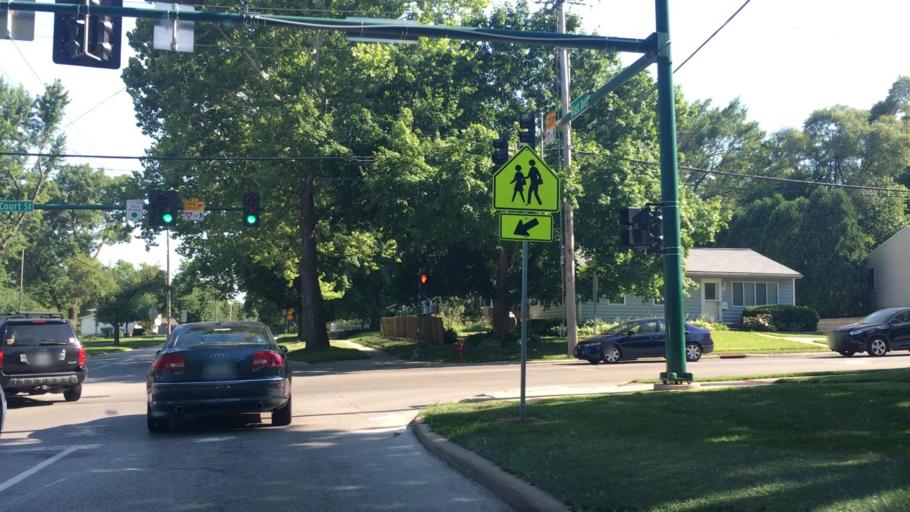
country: US
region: Iowa
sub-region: Johnson County
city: Iowa City
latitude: 41.6570
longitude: -91.5021
